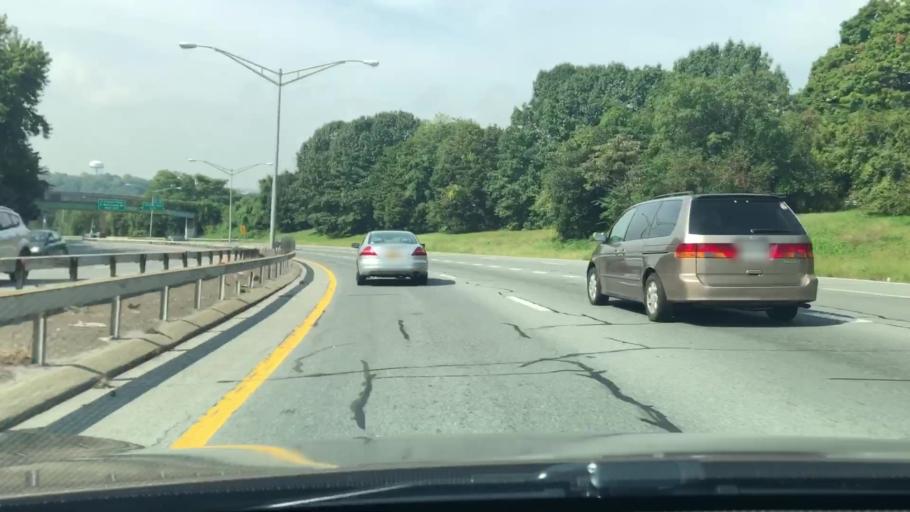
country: US
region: New York
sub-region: Westchester County
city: Bronxville
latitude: 40.9348
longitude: -73.8652
